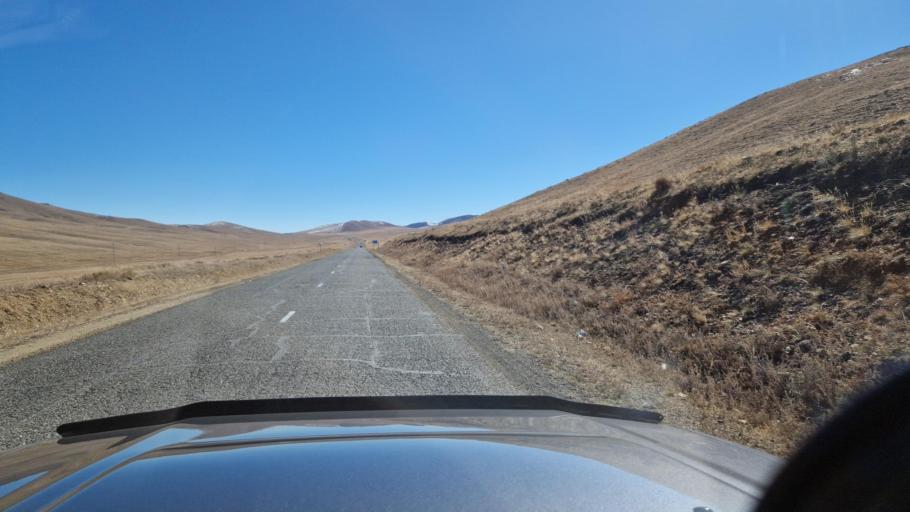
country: MN
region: Hentiy
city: Modot
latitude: 47.8050
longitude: 108.8136
